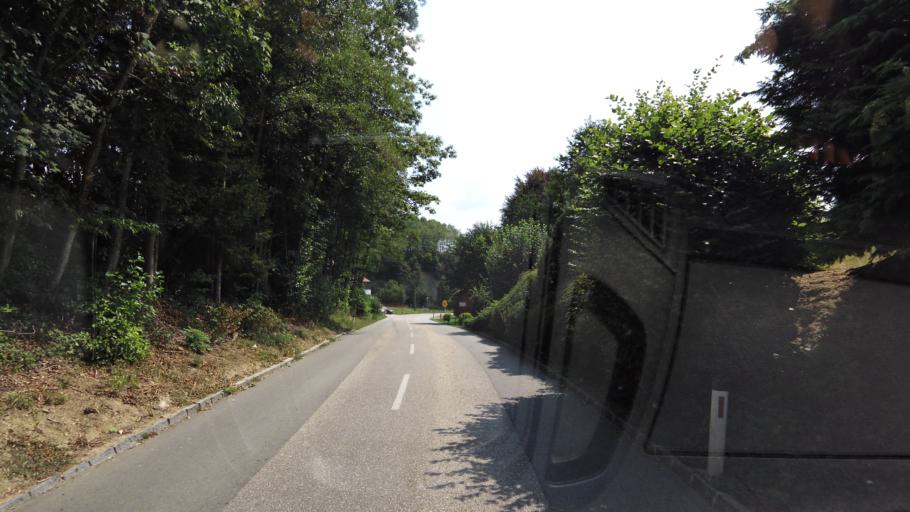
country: AT
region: Upper Austria
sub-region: Politischer Bezirk Ried im Innkreis
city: Waldzell
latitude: 48.1701
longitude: 13.4166
